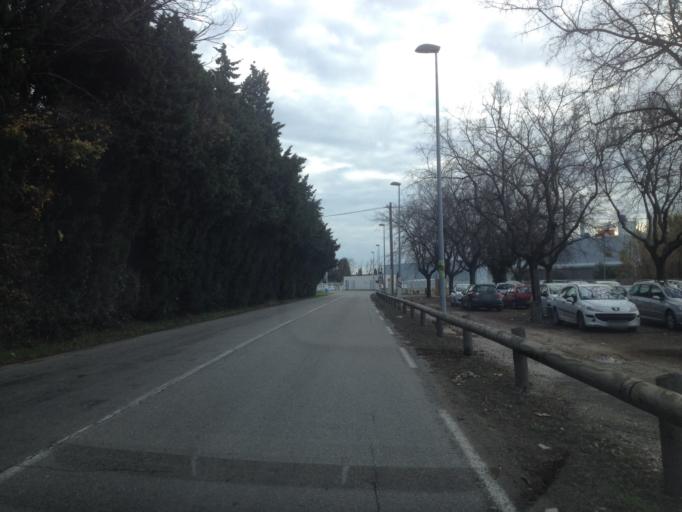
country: FR
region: Provence-Alpes-Cote d'Azur
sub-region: Departement du Vaucluse
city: Sorgues
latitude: 43.9924
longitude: 4.8646
